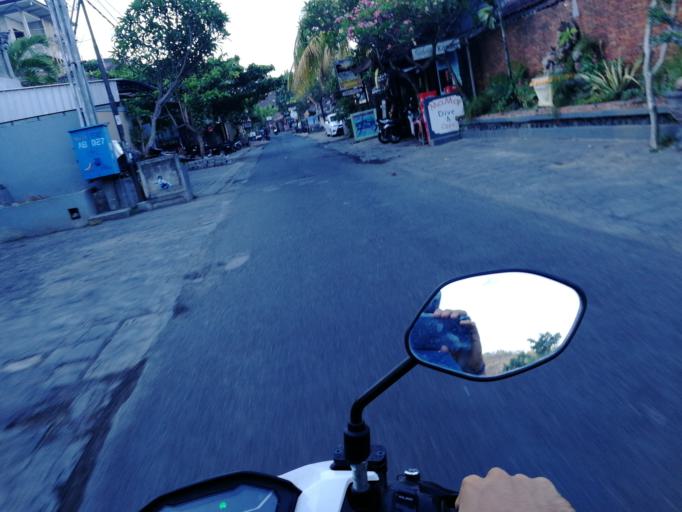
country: ID
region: Bali
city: Biaslantang Kaler
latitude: -8.3377
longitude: 115.6588
